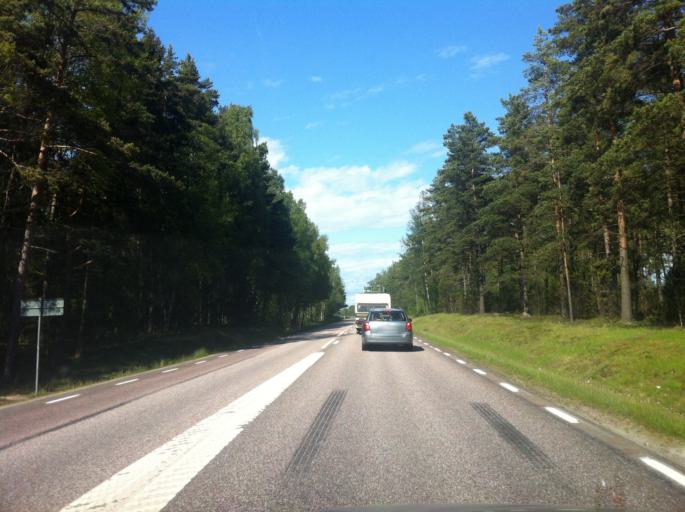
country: SE
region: Vaestra Goetaland
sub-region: Gullspangs Kommun
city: Gullspang
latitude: 59.1025
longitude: 14.1693
